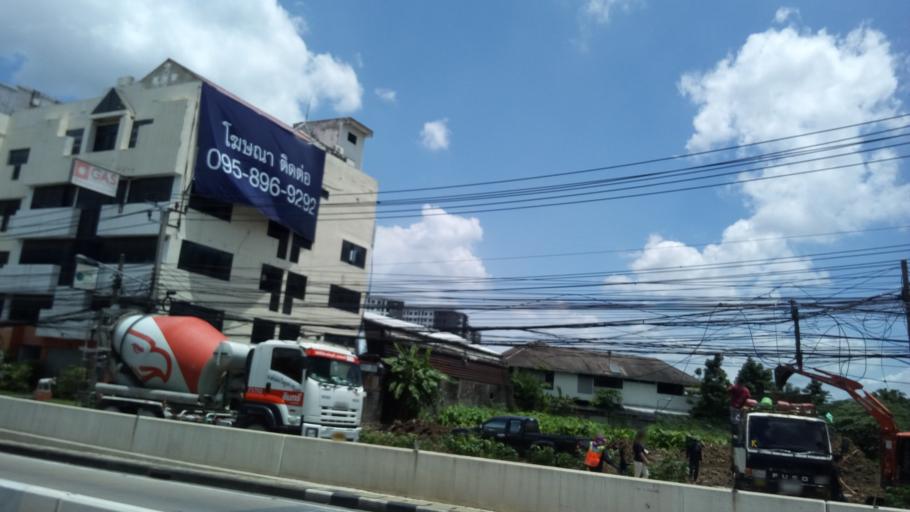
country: TH
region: Bangkok
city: Lak Si
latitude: 13.8783
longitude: 100.5984
